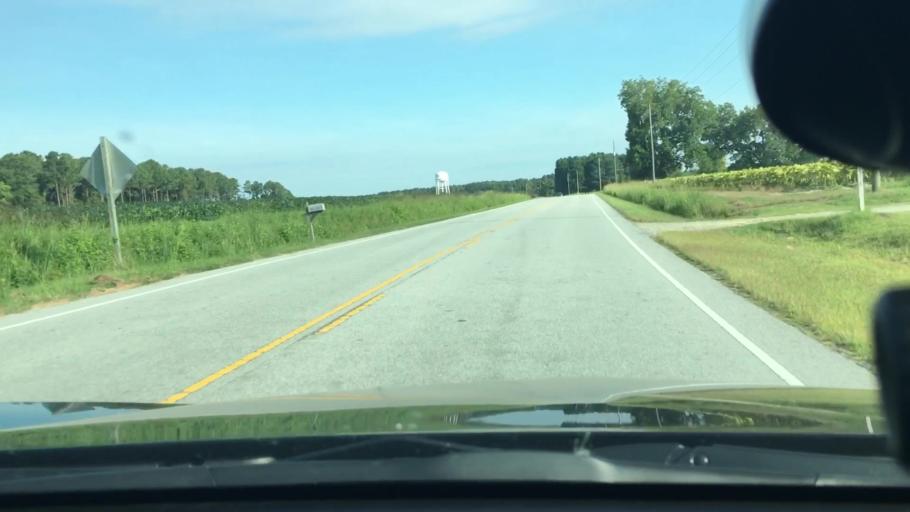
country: US
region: North Carolina
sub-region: Pitt County
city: Farmville
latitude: 35.7042
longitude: -77.5174
